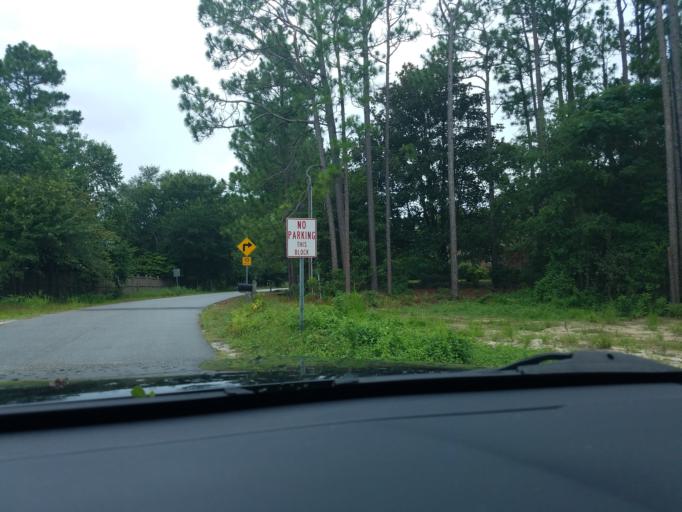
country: US
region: North Carolina
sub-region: New Hanover County
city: Kings Grant
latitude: 34.2370
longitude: -77.8613
